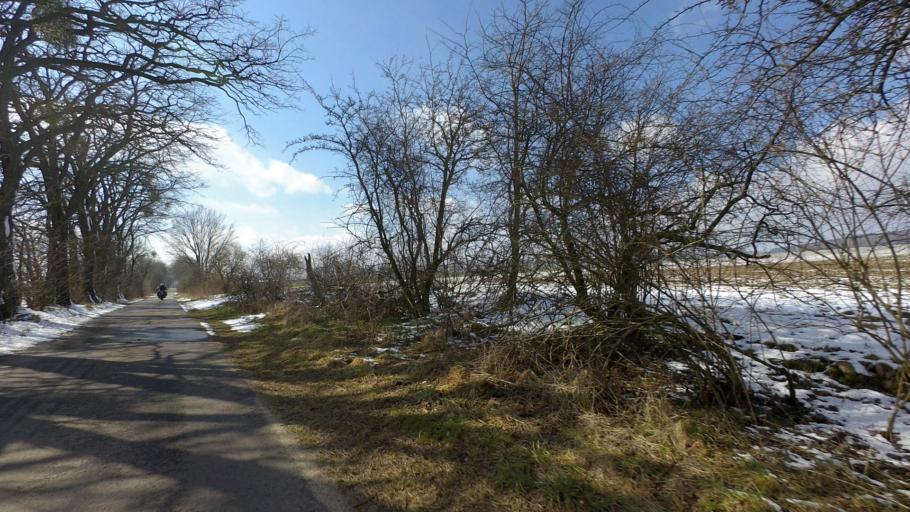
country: DE
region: Brandenburg
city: Werftpfuhl
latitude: 52.7022
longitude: 13.7829
